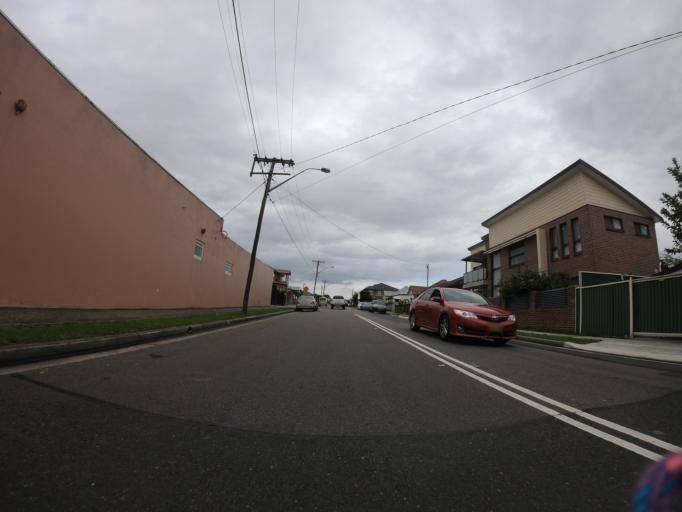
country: AU
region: New South Wales
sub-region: Parramatta
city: Granville
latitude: -33.8460
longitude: 151.0098
